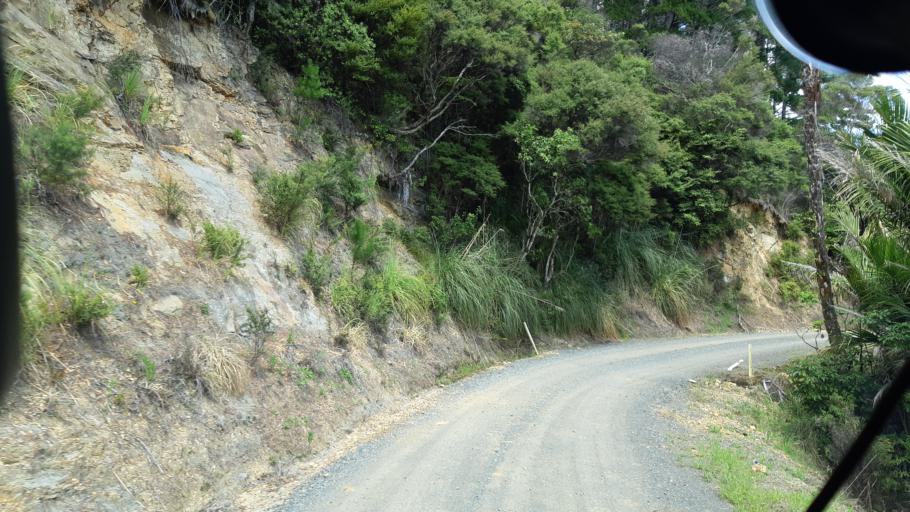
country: NZ
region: Northland
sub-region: Far North District
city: Kaitaia
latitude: -35.2253
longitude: 173.3122
